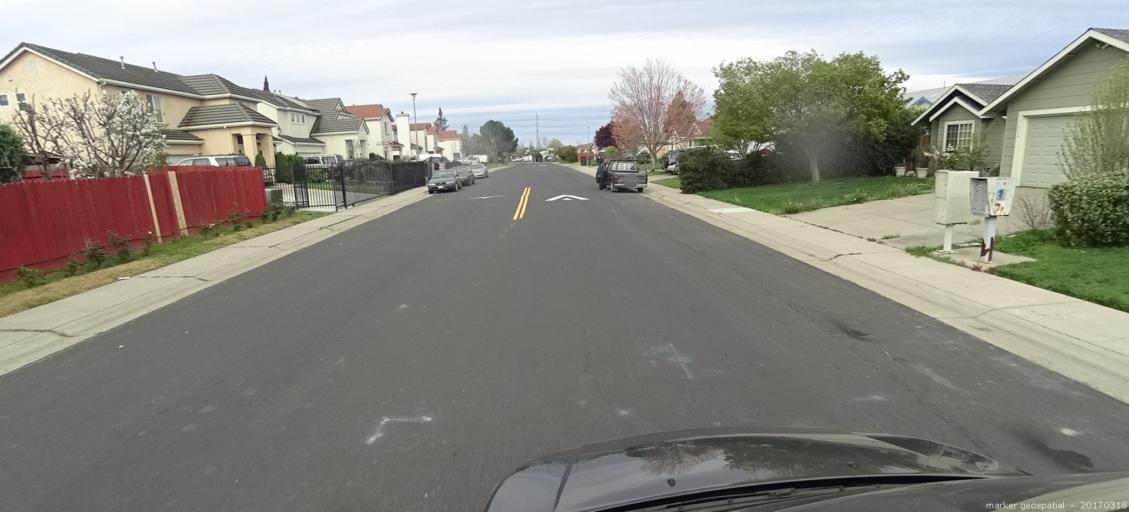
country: US
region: California
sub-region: Sacramento County
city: Parkway
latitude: 38.4831
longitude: -121.4619
